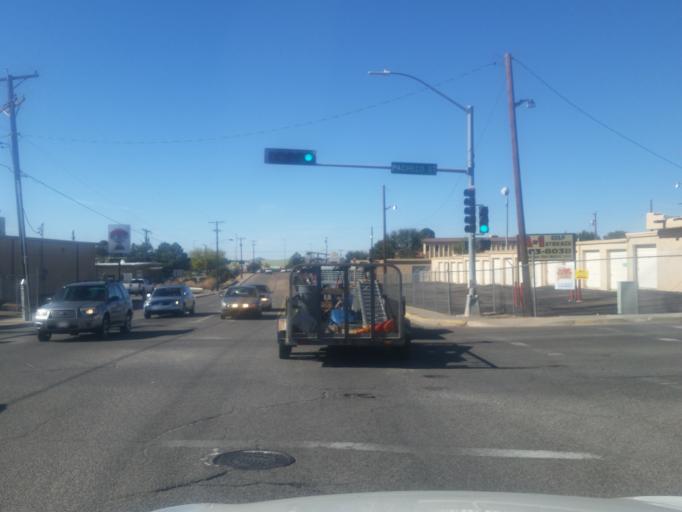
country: US
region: New Mexico
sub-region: Santa Fe County
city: Santa Fe
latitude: 35.6618
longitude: -105.9596
